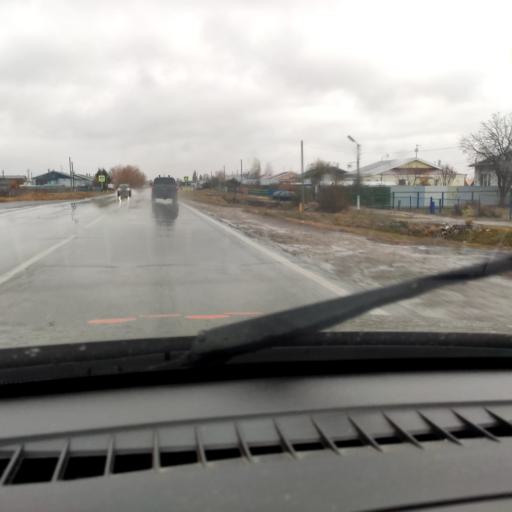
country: RU
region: Samara
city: Tol'yatti
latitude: 53.6373
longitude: 49.2988
